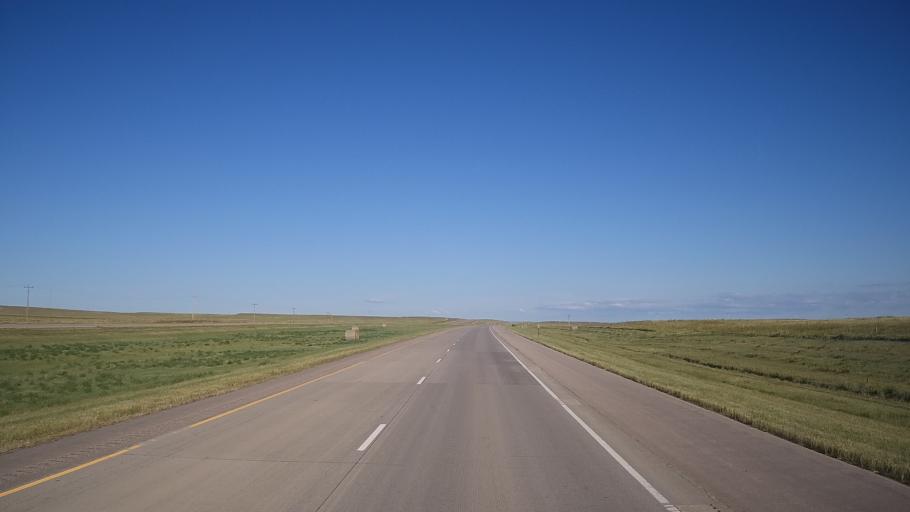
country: US
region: South Dakota
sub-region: Haakon County
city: Philip
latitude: 43.8621
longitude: -101.9458
